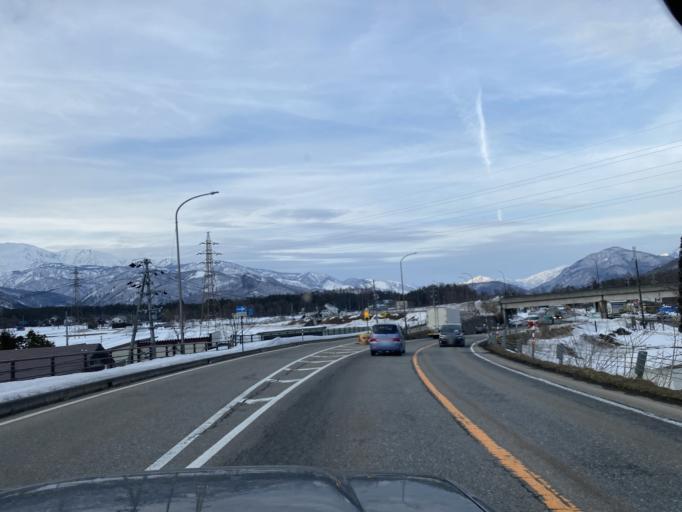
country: JP
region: Nagano
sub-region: Kitaazumi Gun
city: Hakuba
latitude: 36.6722
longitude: 137.8501
